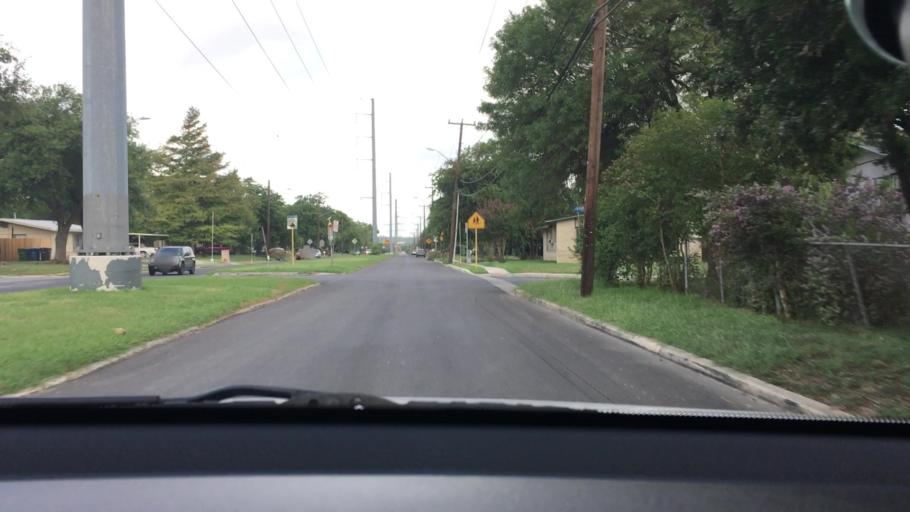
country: US
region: Texas
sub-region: Bexar County
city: Windcrest
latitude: 29.5033
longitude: -98.4018
